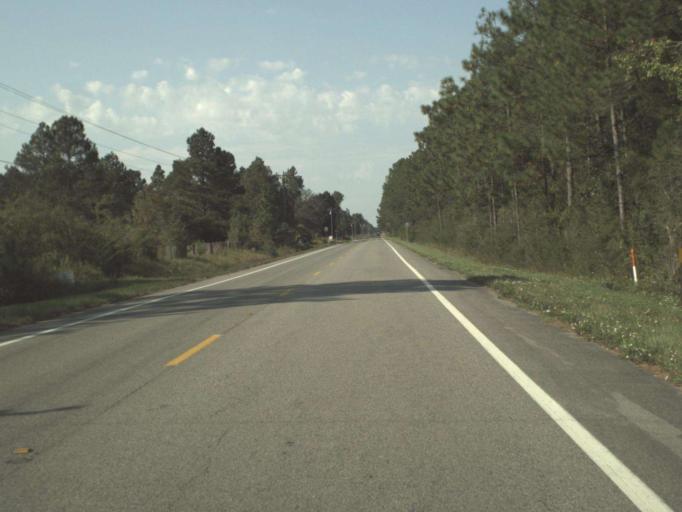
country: US
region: Florida
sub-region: Gulf County
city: Wewahitchka
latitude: 30.0322
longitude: -85.1819
